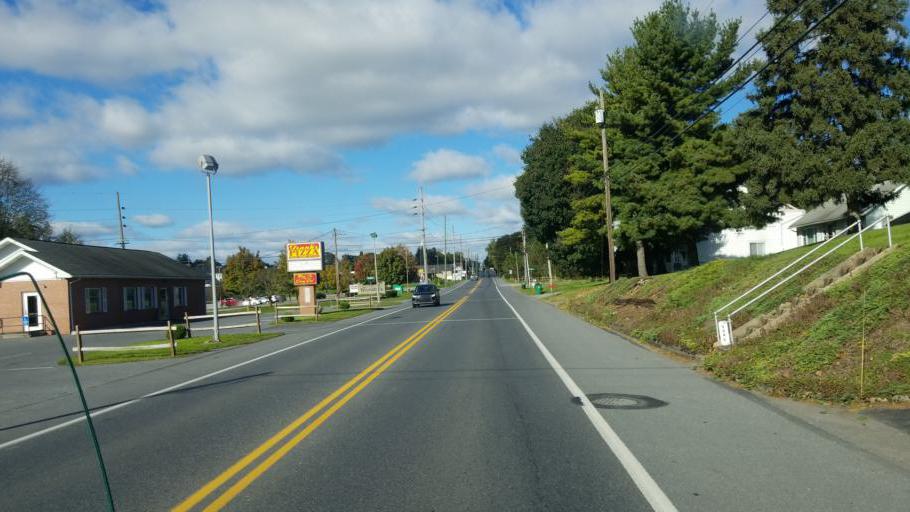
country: US
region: Pennsylvania
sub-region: Franklin County
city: Waynesboro
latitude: 39.7680
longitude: -77.6217
